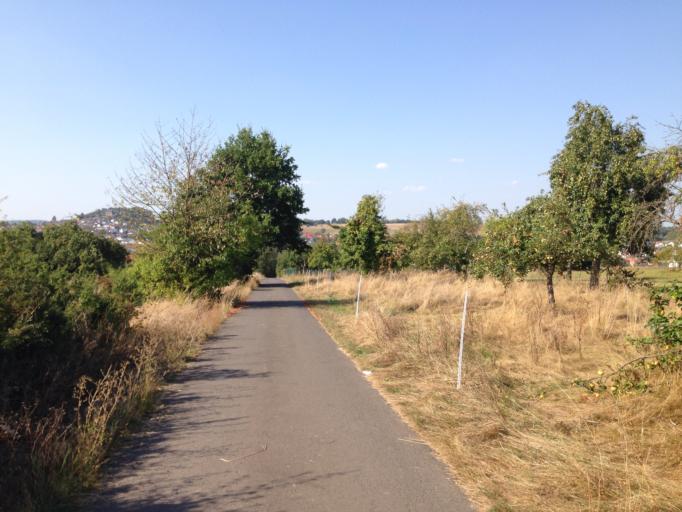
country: DE
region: Hesse
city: Staufenberg
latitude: 50.6532
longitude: 8.7454
